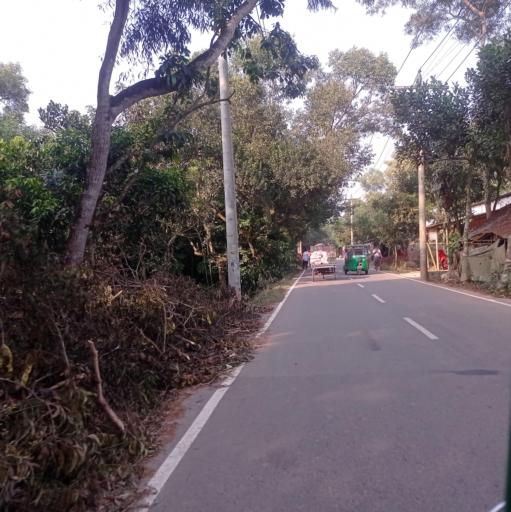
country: BD
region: Dhaka
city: Bhairab Bazar
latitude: 24.0665
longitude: 90.8415
